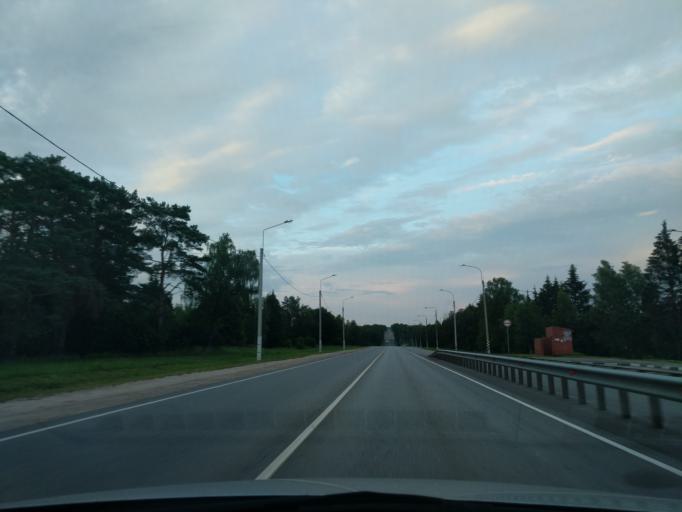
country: RU
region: Kaluga
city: Maloyaroslavets
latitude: 55.0016
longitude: 36.4039
